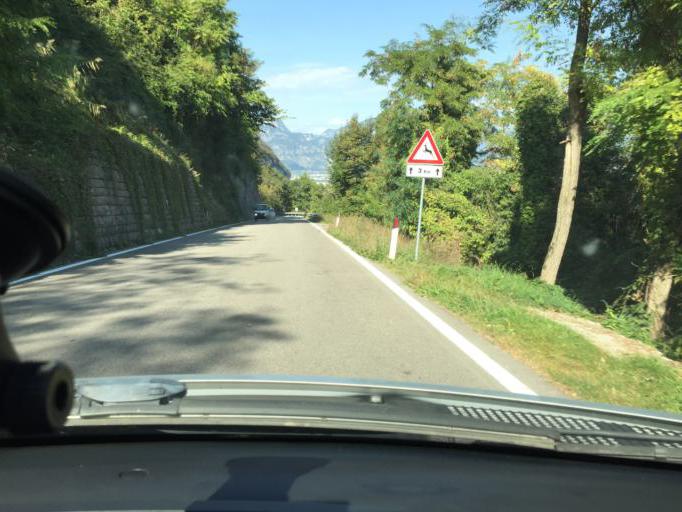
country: IT
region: Trentino-Alto Adige
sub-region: Provincia di Trento
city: Trento
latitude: 46.0700
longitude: 11.0951
